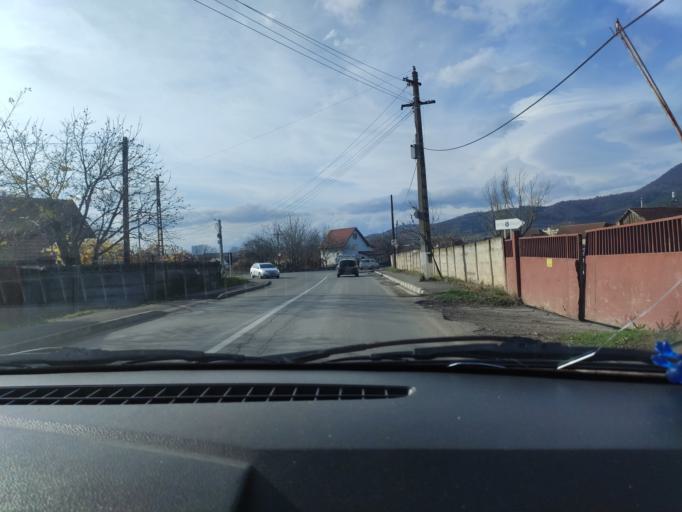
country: RO
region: Brasov
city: Codlea
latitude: 45.7047
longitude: 25.4571
